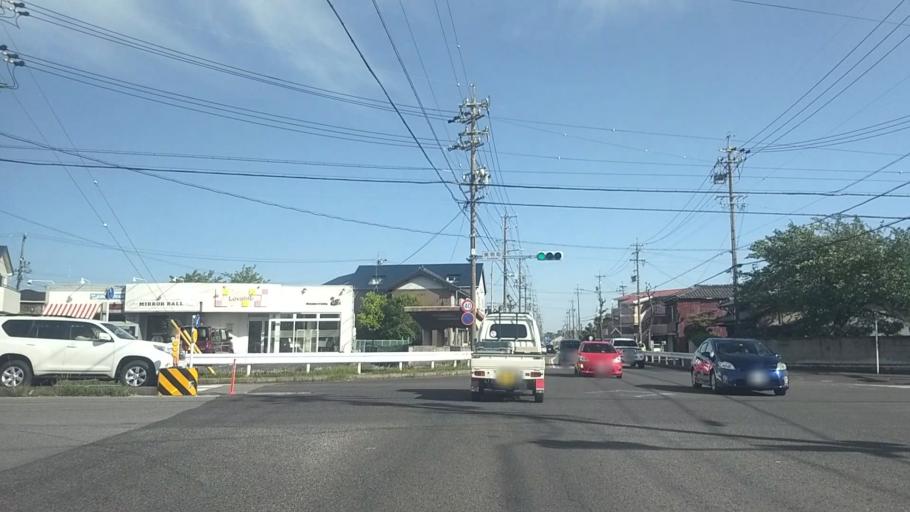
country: JP
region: Aichi
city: Anjo
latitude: 34.9502
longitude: 137.0949
